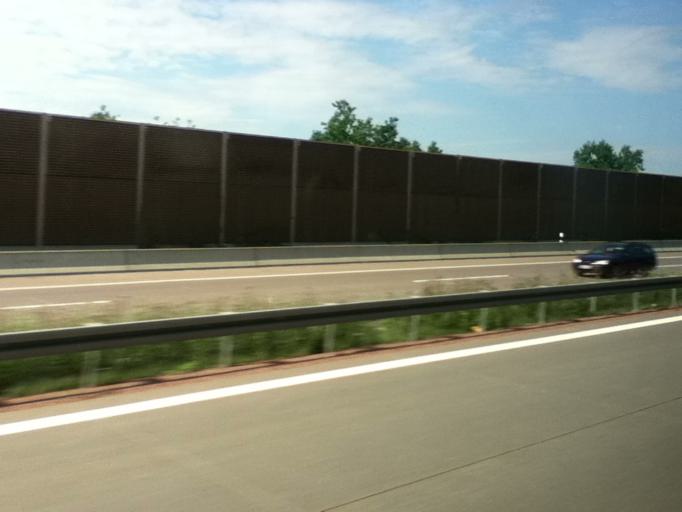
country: DE
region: Saxony
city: Hohenstein-Ernstthal
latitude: 50.8136
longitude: 12.6751
